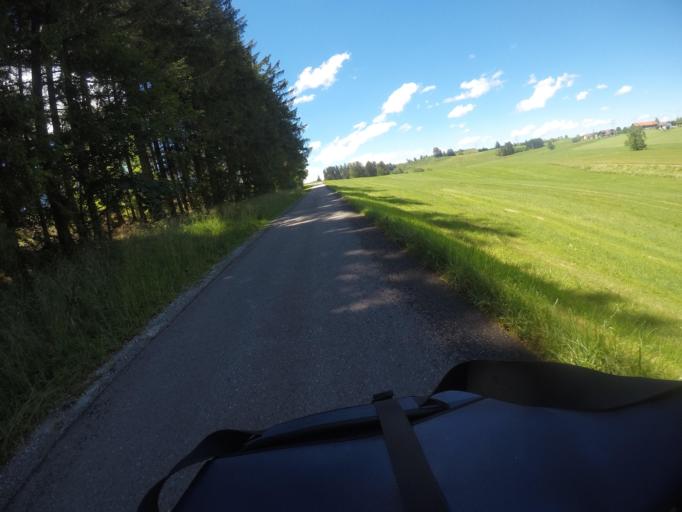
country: DE
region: Bavaria
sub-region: Swabia
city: Rosshaupten
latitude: 47.6775
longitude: 10.7470
